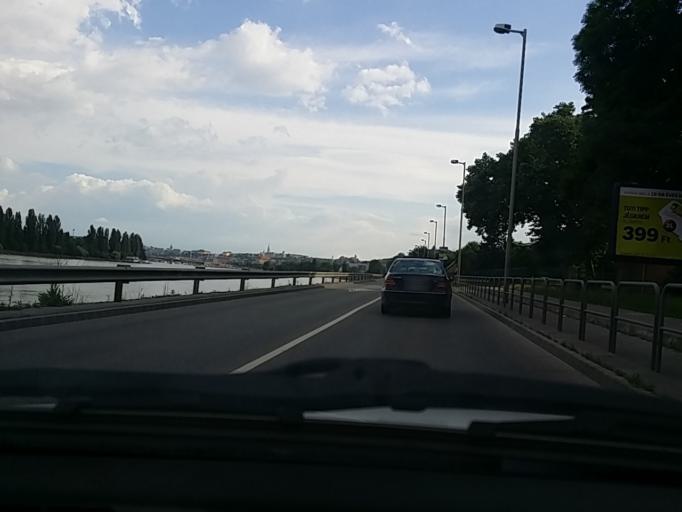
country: HU
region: Budapest
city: Budapest III. keruelet
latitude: 47.5293
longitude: 19.0421
